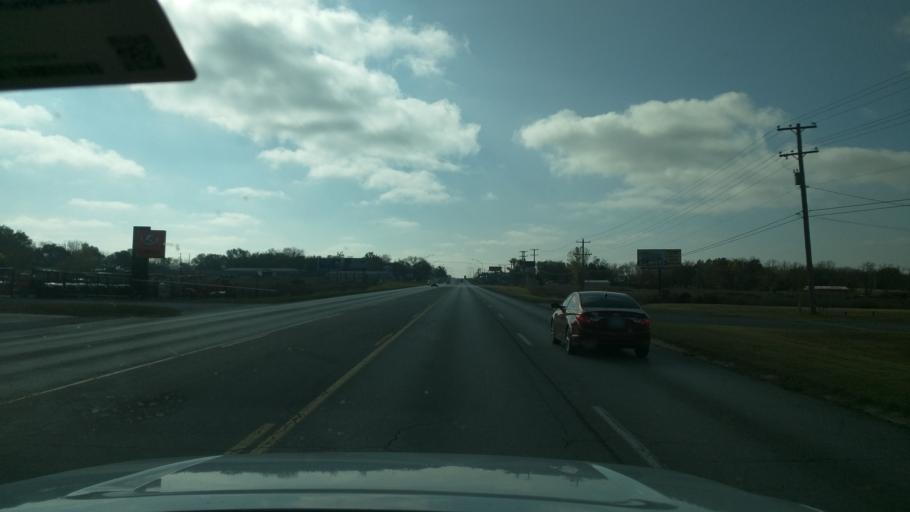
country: US
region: Oklahoma
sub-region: Washington County
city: Dewey
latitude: 36.7744
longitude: -95.9356
